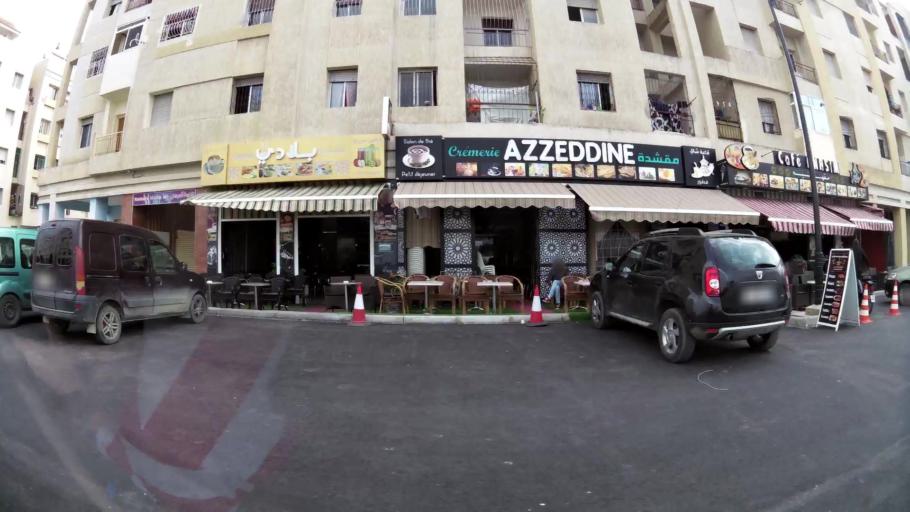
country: MA
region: Tanger-Tetouan
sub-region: Tanger-Assilah
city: Boukhalef
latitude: 35.7372
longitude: -5.8863
